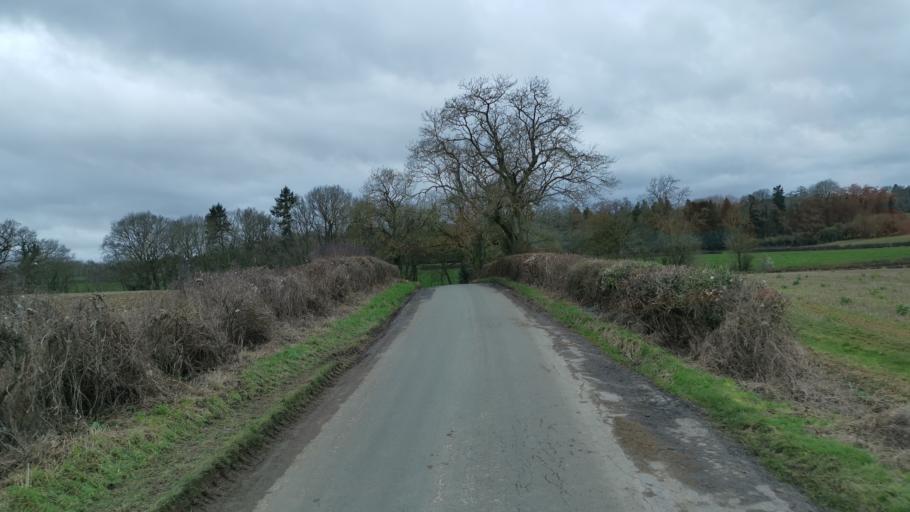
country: GB
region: England
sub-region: Oxfordshire
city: Somerton
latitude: 51.9038
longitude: -1.3165
